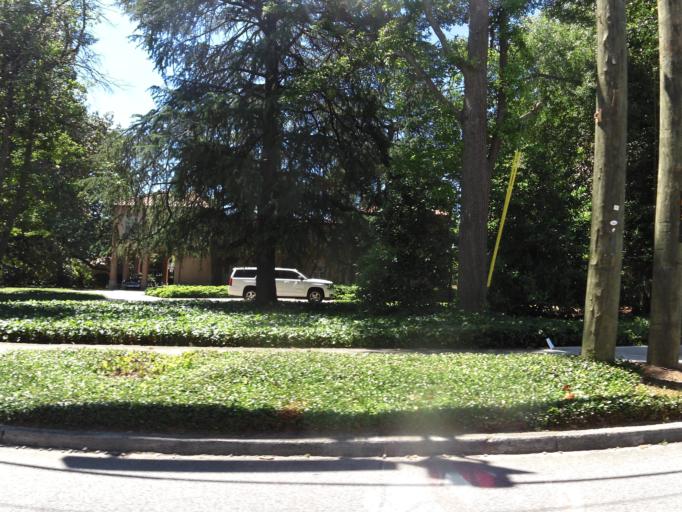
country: US
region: Georgia
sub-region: Richmond County
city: Augusta
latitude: 33.4785
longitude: -82.0272
